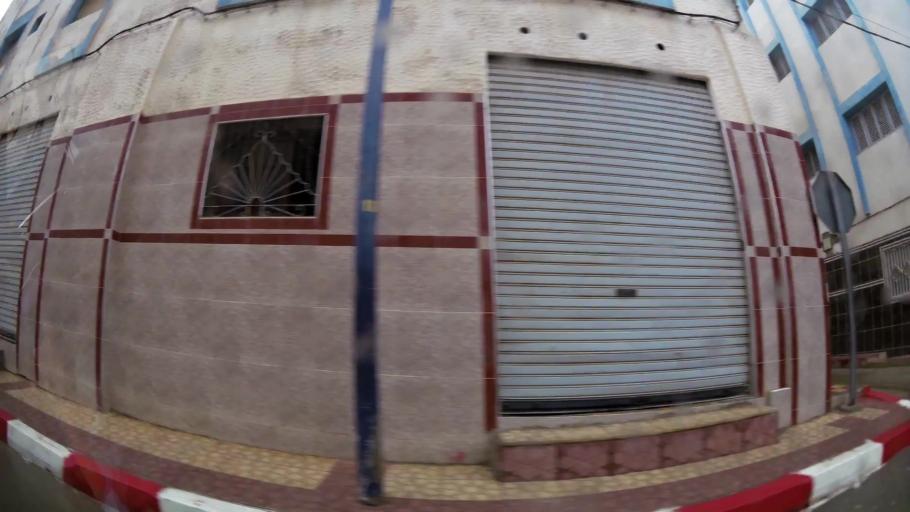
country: MA
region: Taza-Al Hoceima-Taounate
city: Imzourene
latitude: 35.1395
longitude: -3.8534
